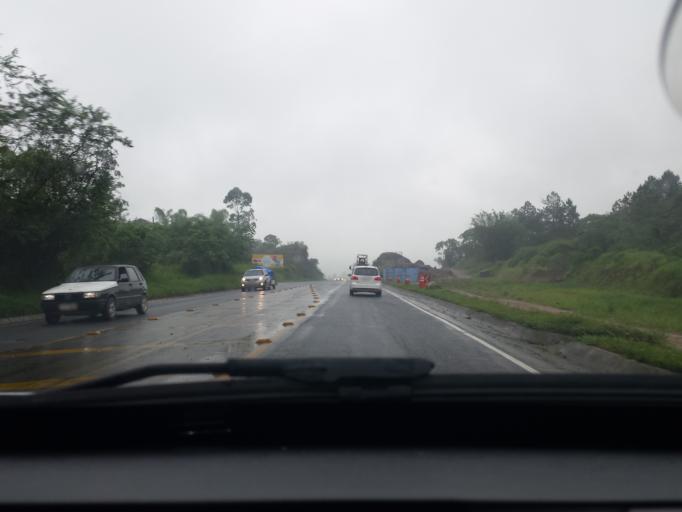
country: BR
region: Santa Catarina
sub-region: Navegantes
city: Navegantes
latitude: -26.8336
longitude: -48.7374
